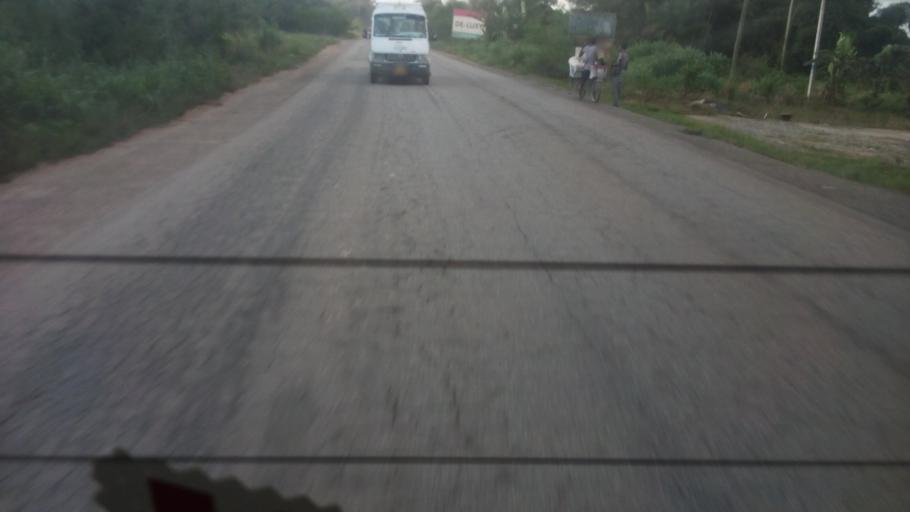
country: GH
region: Western
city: Tarkwa
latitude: 5.2013
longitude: -2.0288
